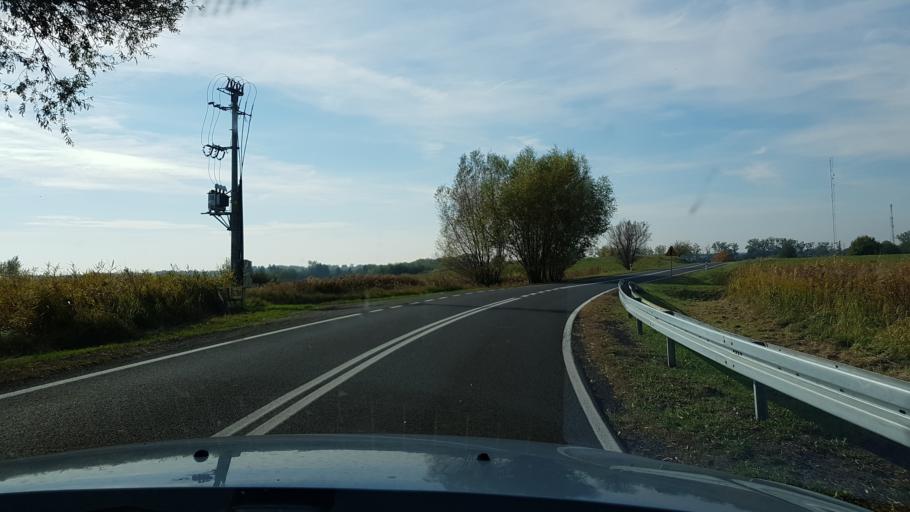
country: PL
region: West Pomeranian Voivodeship
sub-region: Powiat gryfinski
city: Chojna
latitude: 52.9584
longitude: 14.4598
